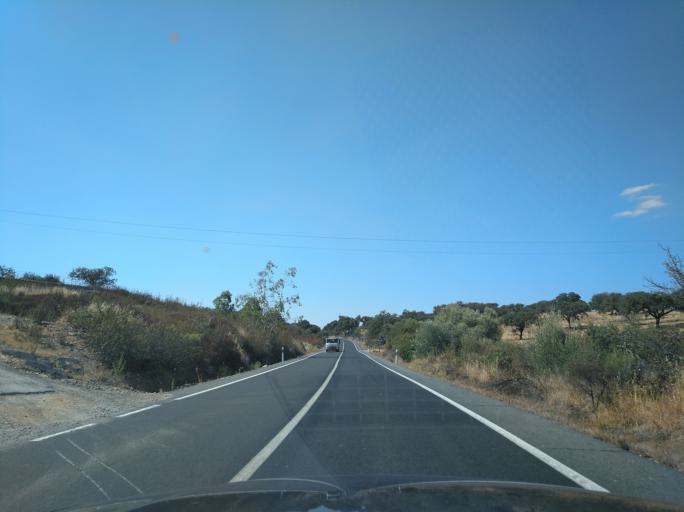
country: ES
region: Andalusia
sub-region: Provincia de Huelva
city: Alosno
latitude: 37.5167
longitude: -7.1324
